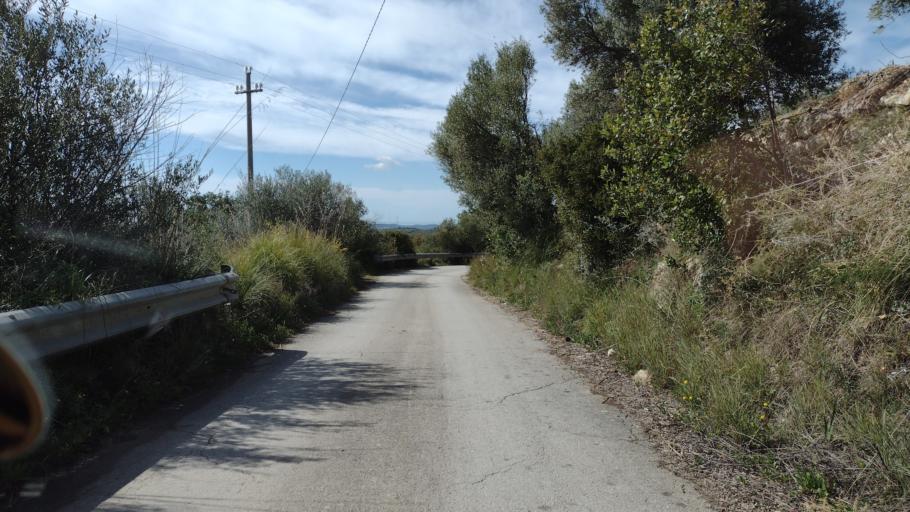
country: IT
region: Sicily
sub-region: Provincia di Siracusa
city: Noto
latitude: 36.9051
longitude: 15.0245
